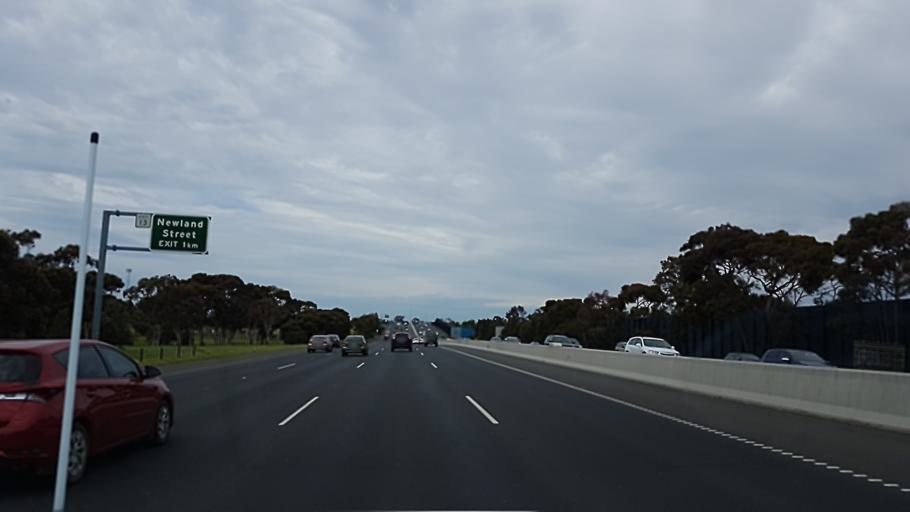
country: AU
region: Victoria
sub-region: Hobsons Bay
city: Laverton
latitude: -37.8558
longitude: 144.7786
